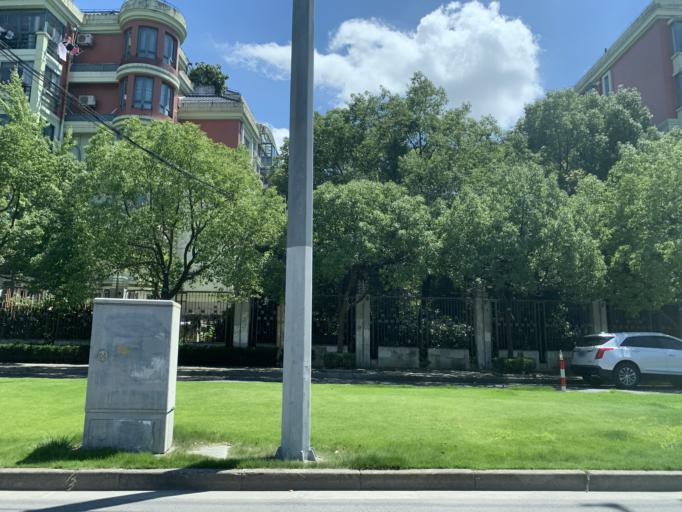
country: CN
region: Shanghai Shi
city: Huamu
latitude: 31.1778
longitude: 121.5343
